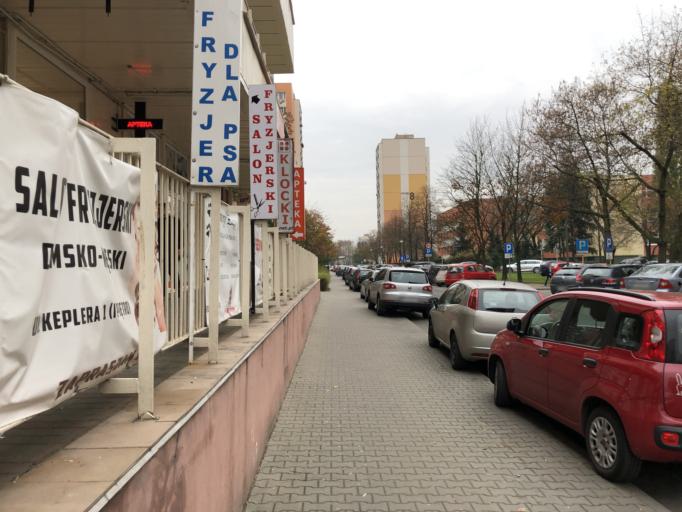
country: PL
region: Greater Poland Voivodeship
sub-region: Powiat poznanski
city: Lubon
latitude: 52.3906
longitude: 16.8641
